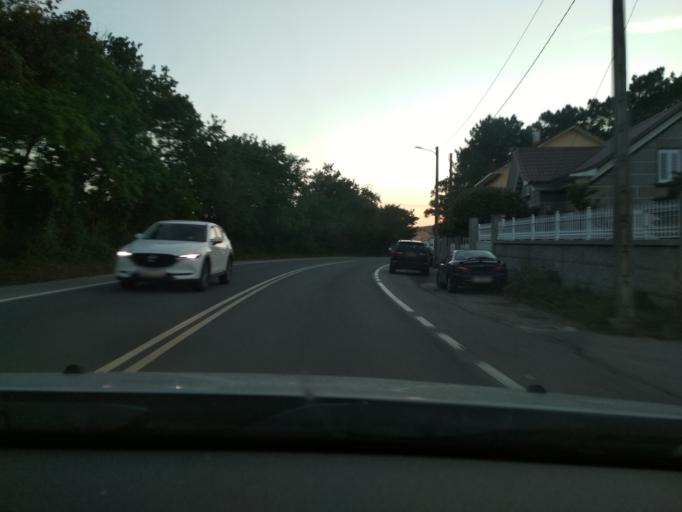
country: ES
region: Galicia
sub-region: Provincia de Pontevedra
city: Catoira
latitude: 42.6699
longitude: -8.7124
